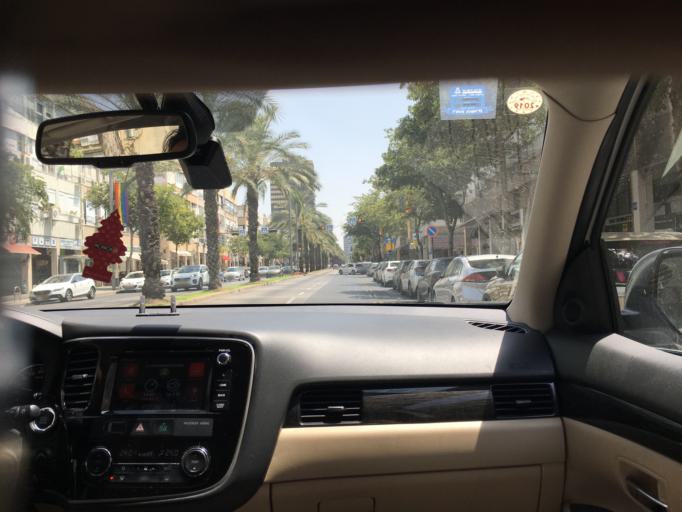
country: IL
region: Tel Aviv
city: Tel Aviv
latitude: 32.0899
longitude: 34.7826
